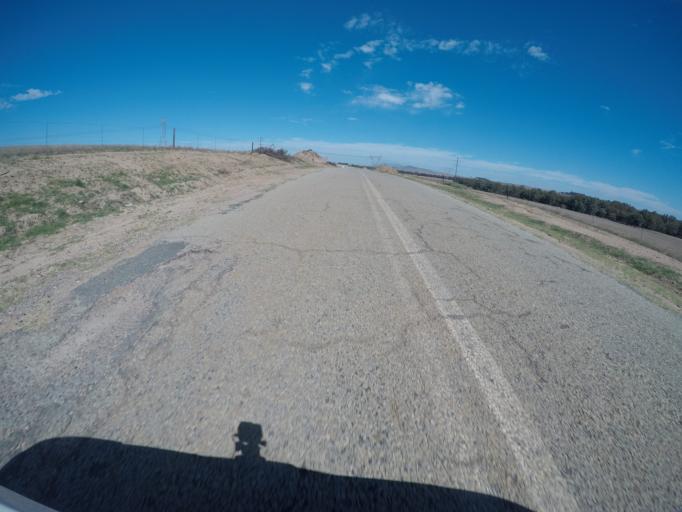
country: ZA
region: Western Cape
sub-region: West Coast District Municipality
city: Malmesbury
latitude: -33.5937
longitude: 18.6443
